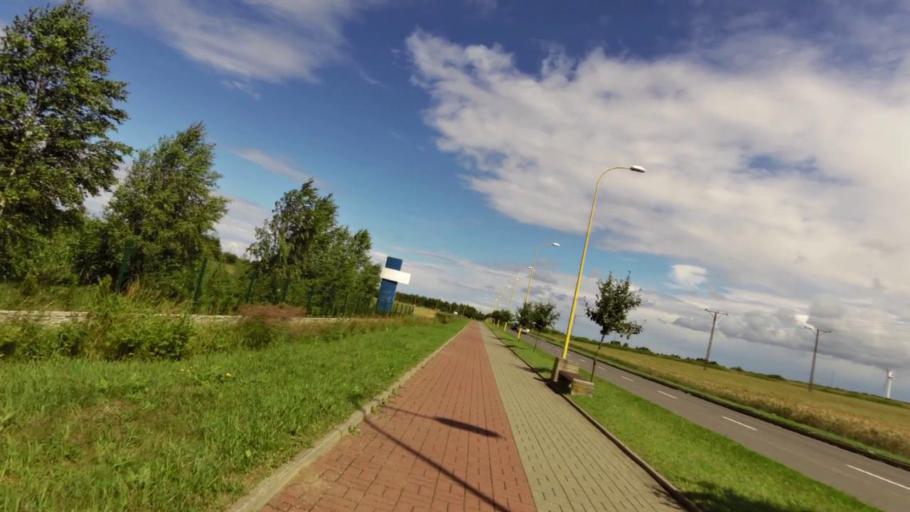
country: PL
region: West Pomeranian Voivodeship
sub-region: Powiat slawienski
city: Darlowo
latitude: 54.4393
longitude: 16.4078
